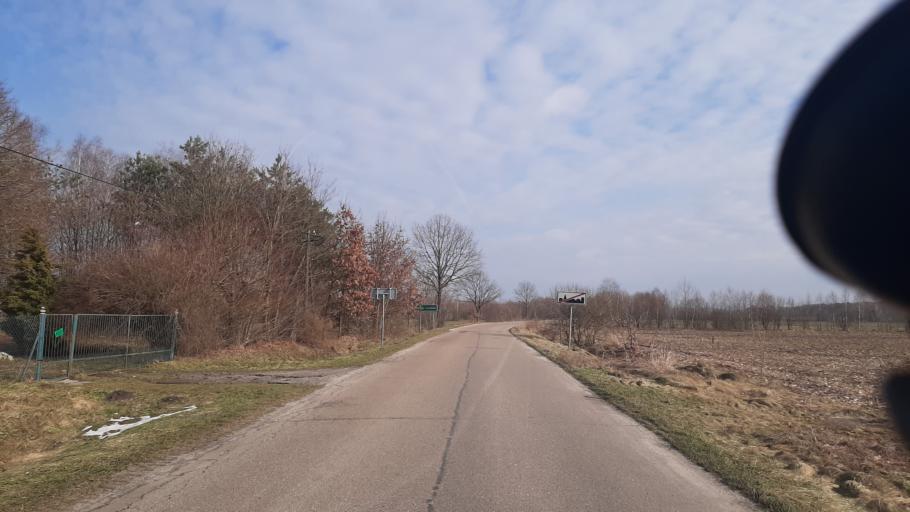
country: PL
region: Lublin Voivodeship
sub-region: Powiat lubartowski
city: Uscimow Stary
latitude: 51.4698
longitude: 22.9710
